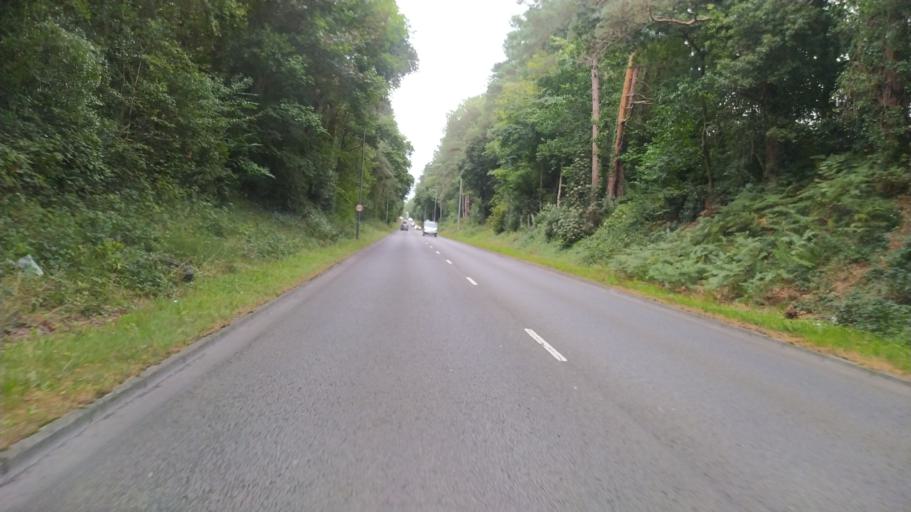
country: GB
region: England
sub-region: Dorset
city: Broadstone
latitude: 50.7571
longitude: -1.9989
